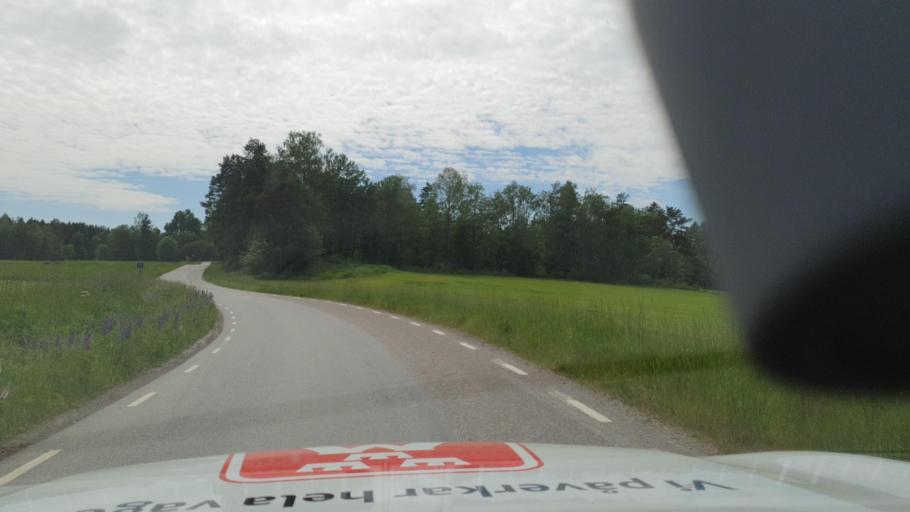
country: SE
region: Vaestra Goetaland
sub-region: Vanersborgs Kommun
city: Vargon
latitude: 58.2836
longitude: 12.5154
